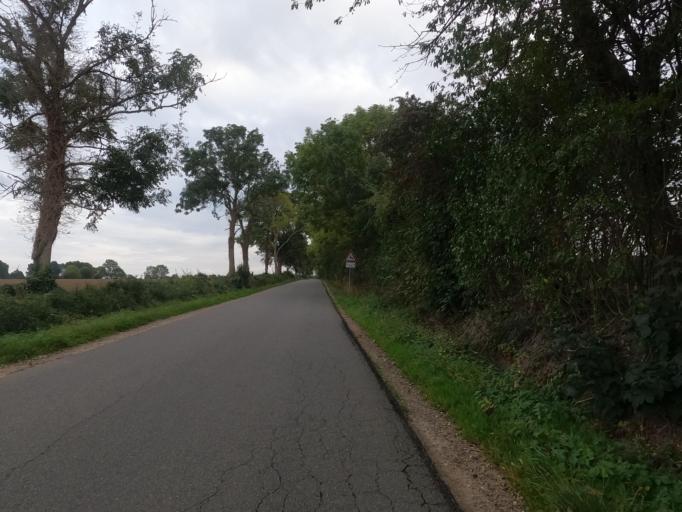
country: DE
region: Schleswig-Holstein
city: Neukirchen
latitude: 54.3184
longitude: 11.0372
